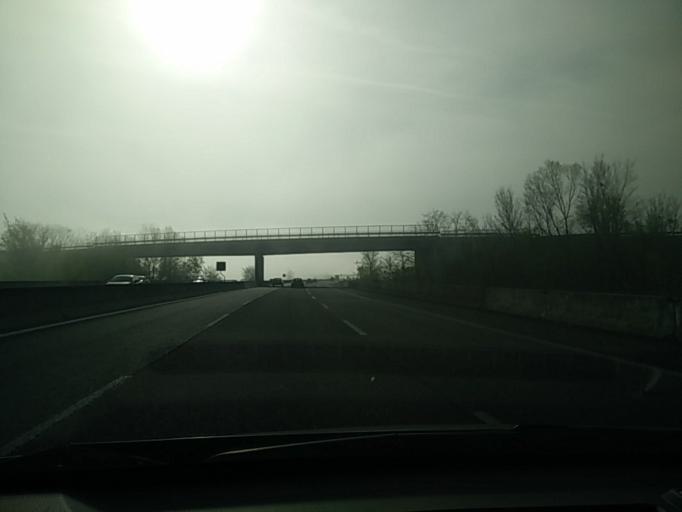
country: IT
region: Emilia-Romagna
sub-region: Provincia di Bologna
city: Osteria Grande
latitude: 44.4536
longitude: 11.5344
